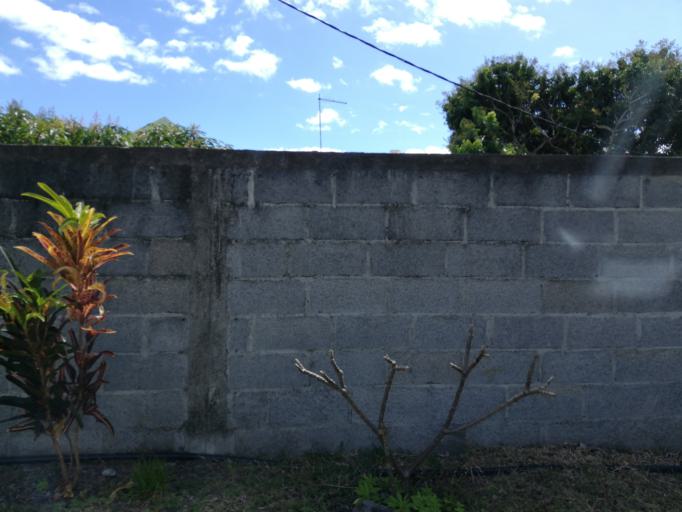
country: MU
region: Plaines Wilhems
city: Ebene
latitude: -20.2341
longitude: 57.4668
